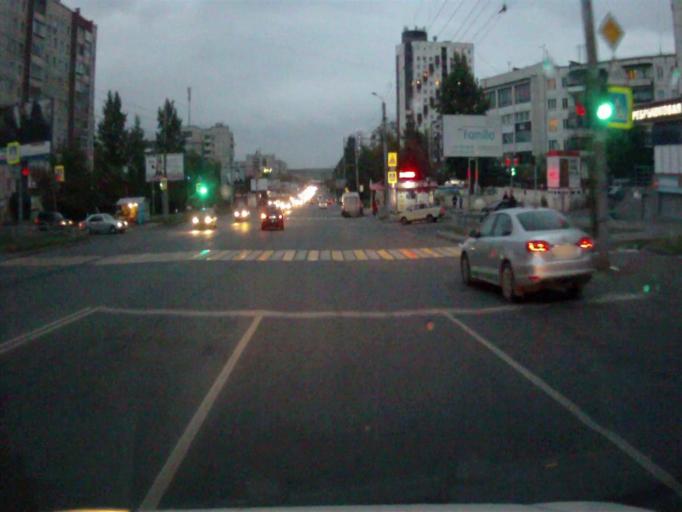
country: RU
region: Chelyabinsk
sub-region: Gorod Chelyabinsk
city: Chelyabinsk
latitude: 55.1845
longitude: 61.3326
